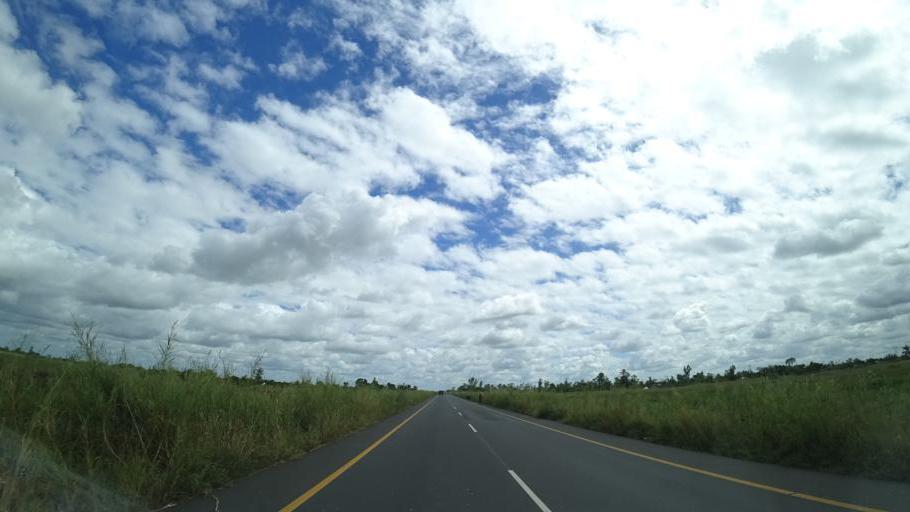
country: MZ
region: Sofala
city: Dondo
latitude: -19.3855
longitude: 34.4109
